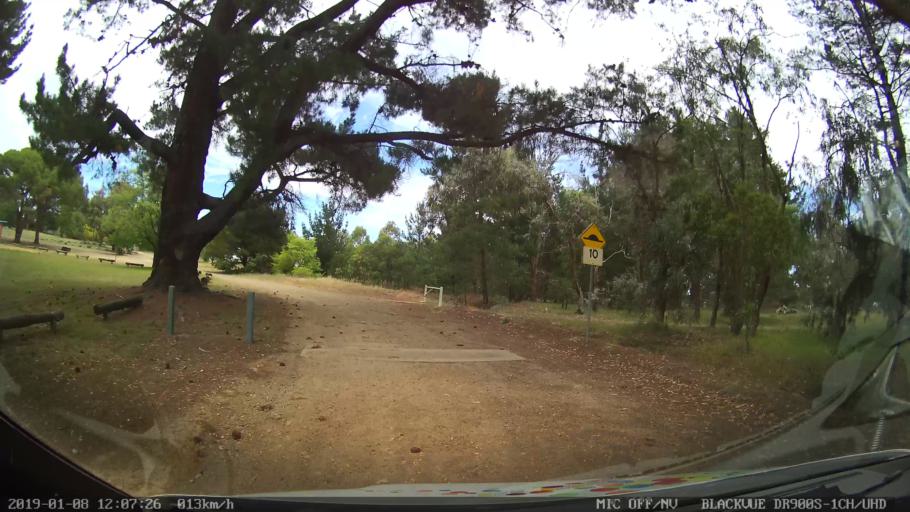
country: AU
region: New South Wales
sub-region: Armidale Dumaresq
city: Armidale
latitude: -30.4273
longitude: 151.5938
